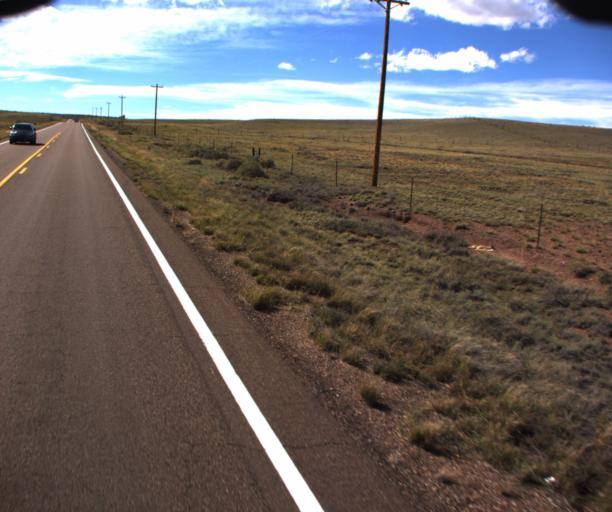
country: US
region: Arizona
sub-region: Apache County
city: Saint Johns
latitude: 34.5091
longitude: -109.4686
